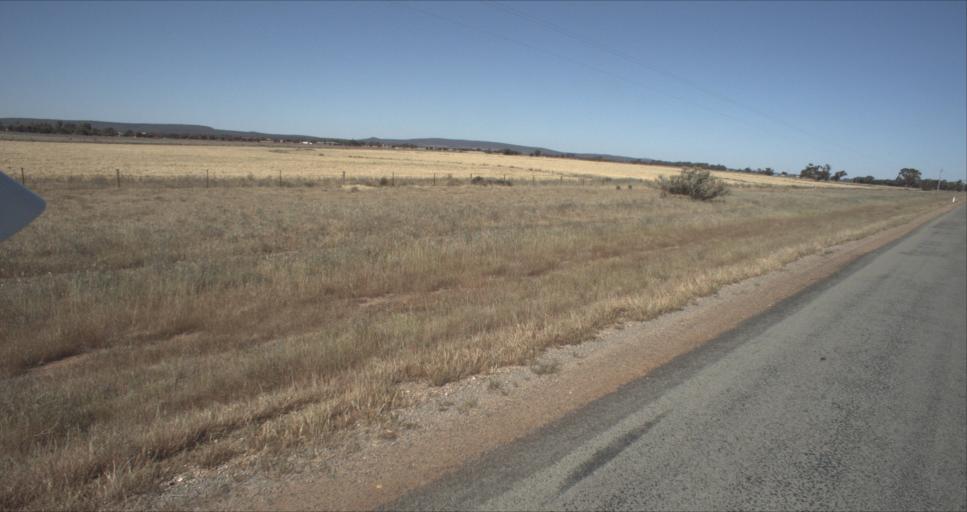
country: AU
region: New South Wales
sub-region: Leeton
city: Leeton
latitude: -34.4938
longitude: 146.3866
